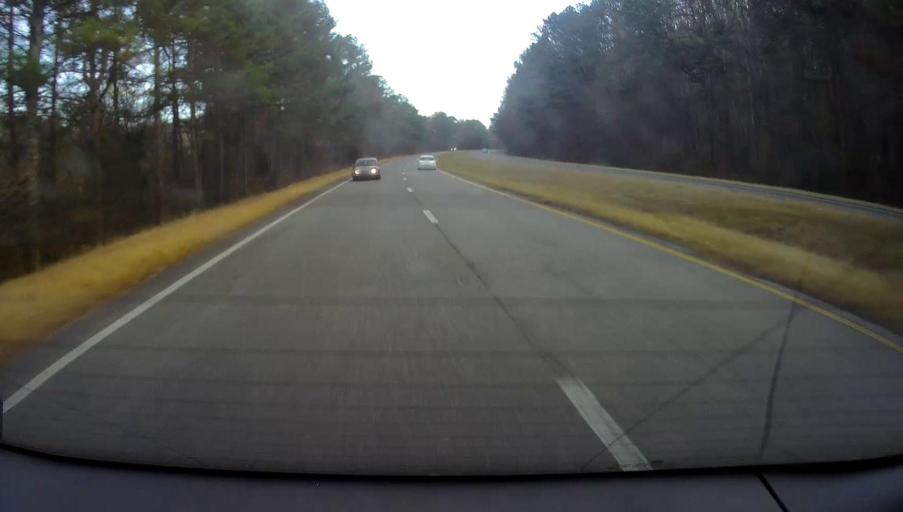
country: US
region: Alabama
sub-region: Etowah County
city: Glencoe
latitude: 33.9408
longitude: -85.9158
